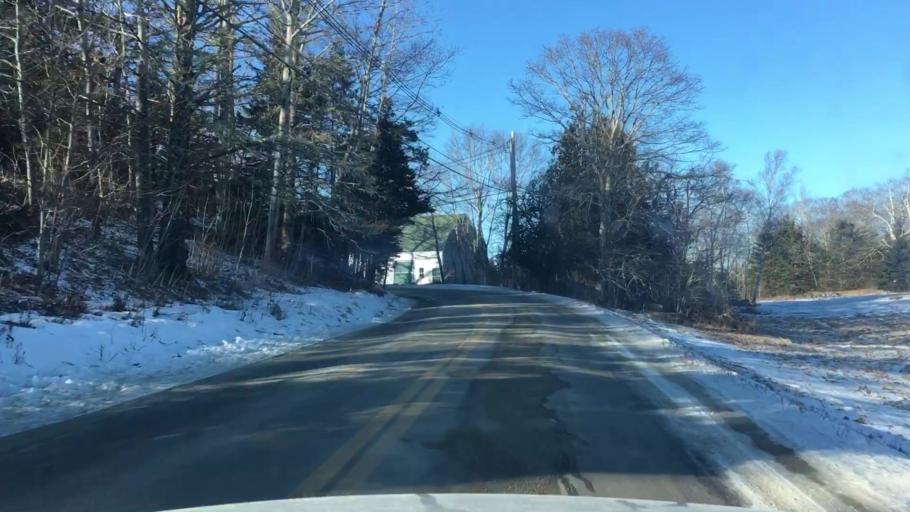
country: US
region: Maine
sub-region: Hancock County
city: Castine
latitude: 44.3484
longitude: -68.7475
